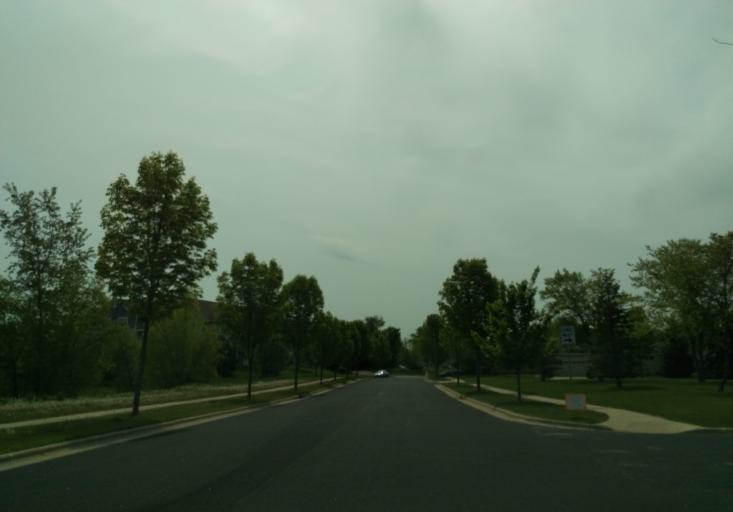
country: US
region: Wisconsin
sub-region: Dane County
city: Cottage Grove
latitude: 43.0873
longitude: -89.2580
